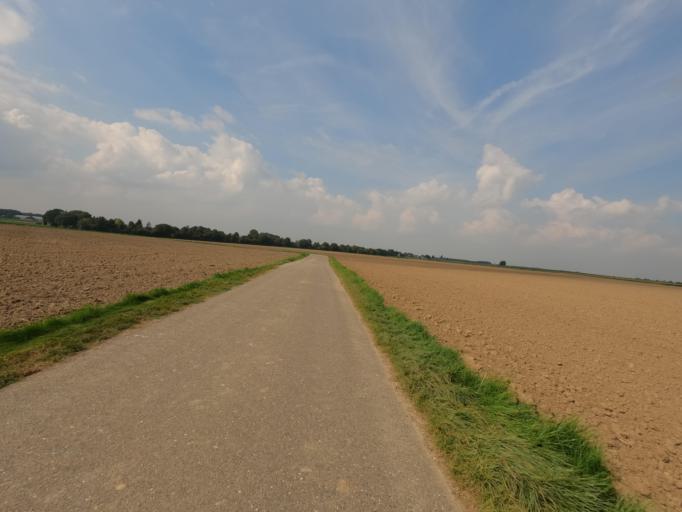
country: DE
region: North Rhine-Westphalia
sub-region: Regierungsbezirk Koln
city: Ubach-Palenberg
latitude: 50.9291
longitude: 6.1283
